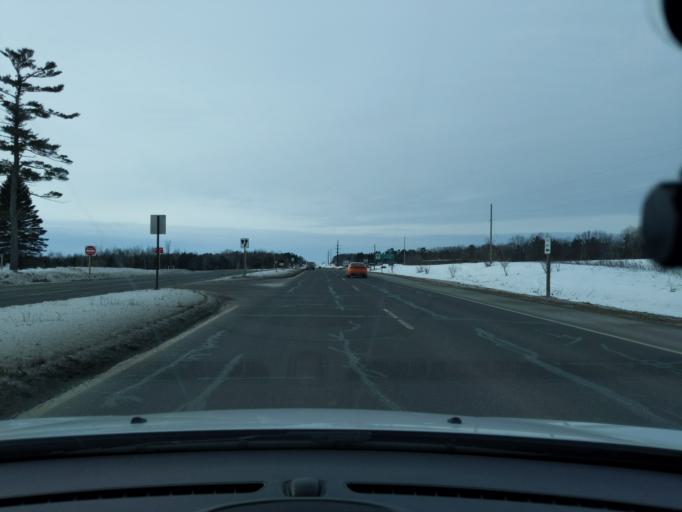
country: US
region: Wisconsin
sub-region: Barron County
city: Turtle Lake
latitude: 45.3955
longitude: -92.1629
